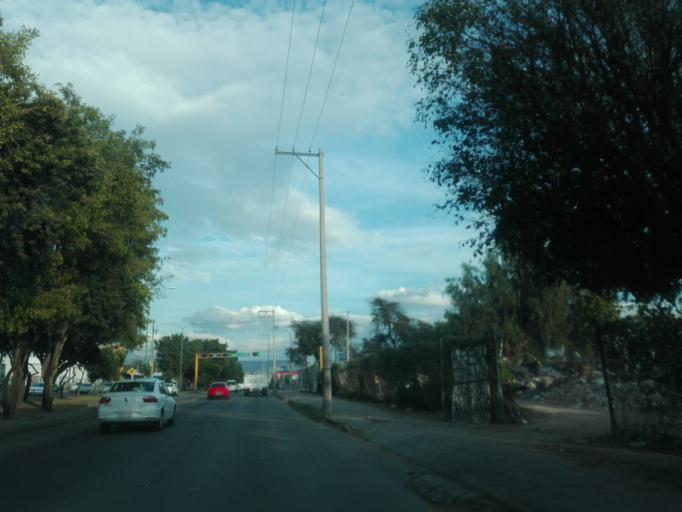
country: MX
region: Guanajuato
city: Leon
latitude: 21.1473
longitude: -101.6819
